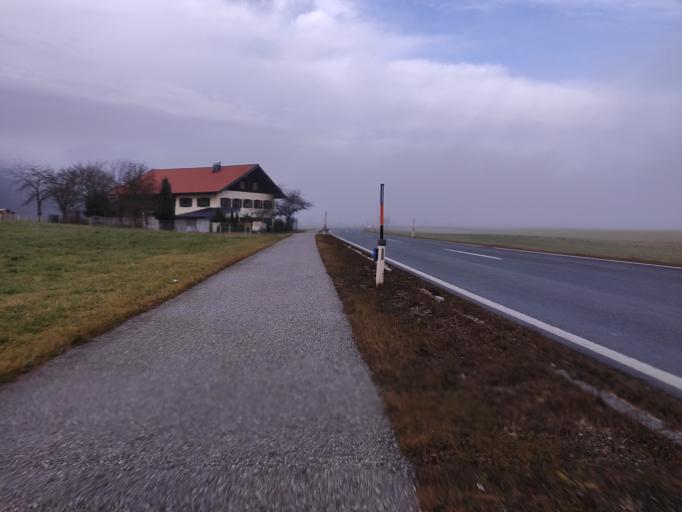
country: AT
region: Upper Austria
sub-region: Politischer Bezirk Vocklabruck
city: Oberhofen am Irrsee
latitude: 47.9631
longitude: 13.2962
